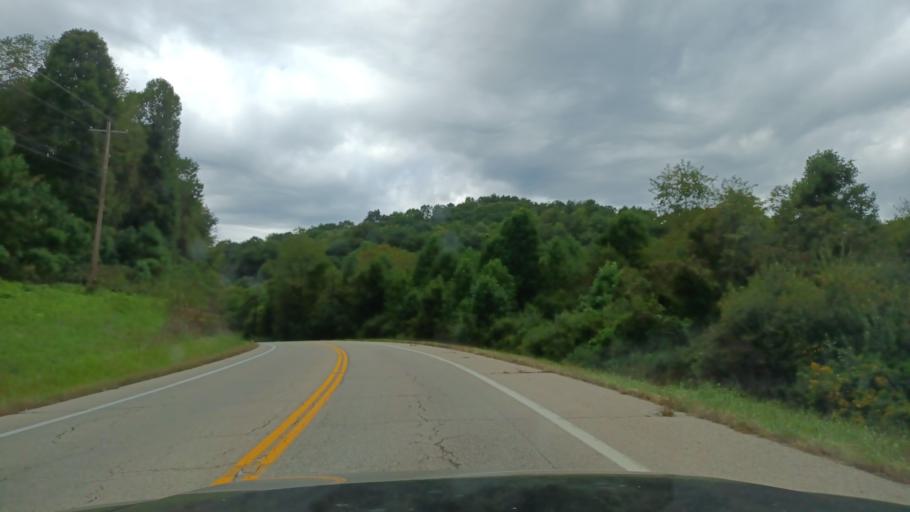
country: US
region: Ohio
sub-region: Vinton County
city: McArthur
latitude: 39.2431
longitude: -82.4545
